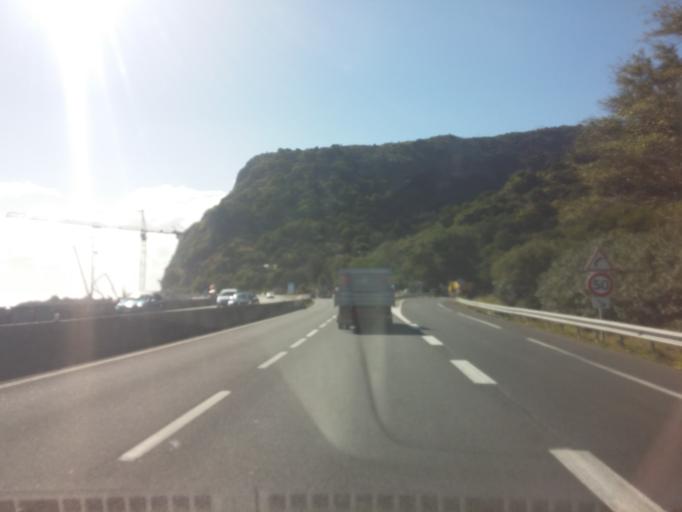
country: RE
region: Reunion
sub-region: Reunion
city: La Possession
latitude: -20.8972
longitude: 55.3743
